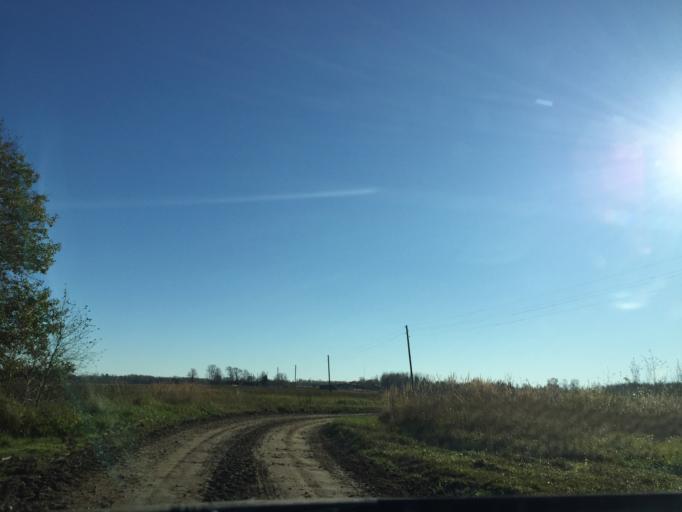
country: LV
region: Skriveri
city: Skriveri
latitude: 56.6566
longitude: 25.1910
